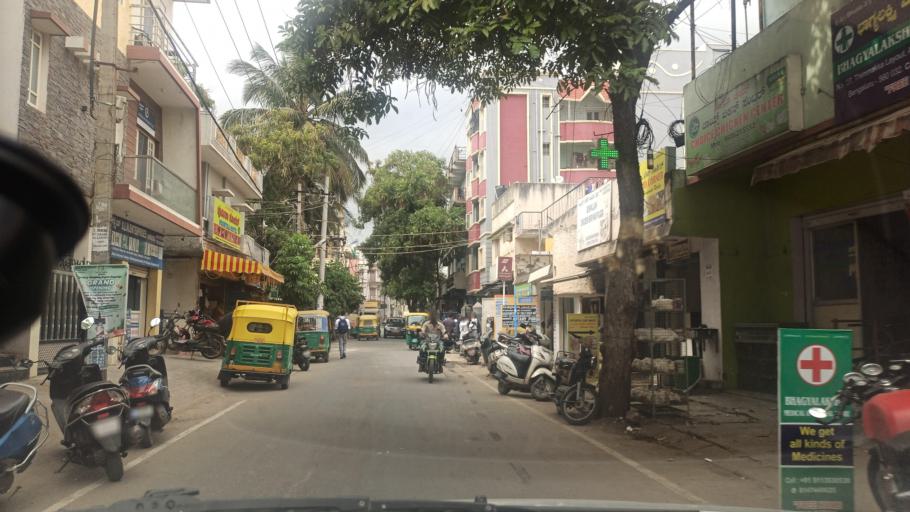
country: IN
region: Karnataka
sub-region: Bangalore Urban
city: Bangalore
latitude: 13.0353
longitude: 77.6000
